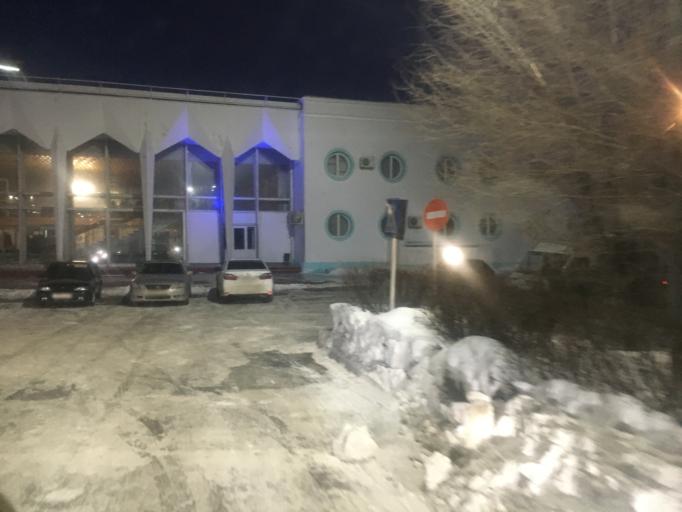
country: KZ
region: Batys Qazaqstan
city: Oral
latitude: 51.1537
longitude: 51.5378
